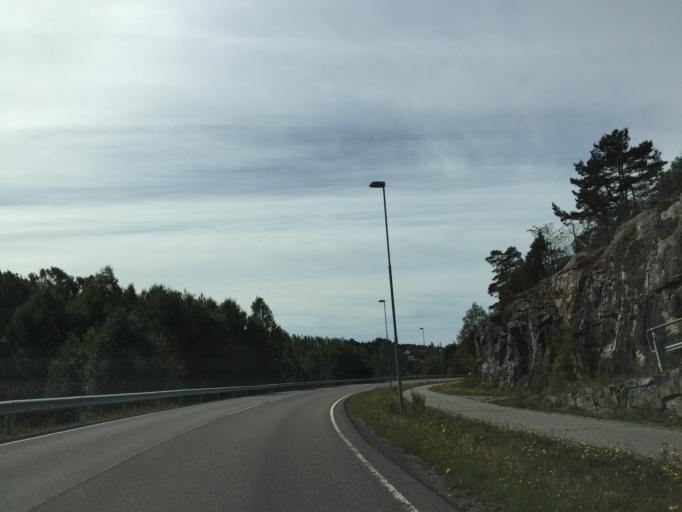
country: NO
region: Ostfold
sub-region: Moss
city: Moss
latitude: 59.5199
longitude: 10.6959
